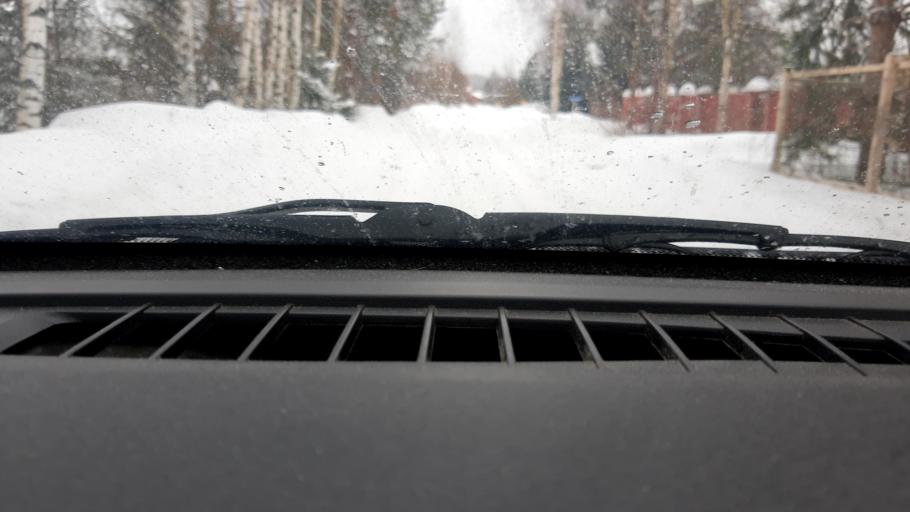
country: RU
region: Moskovskaya
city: Pirogovskiy
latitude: 56.0173
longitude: 37.7259
